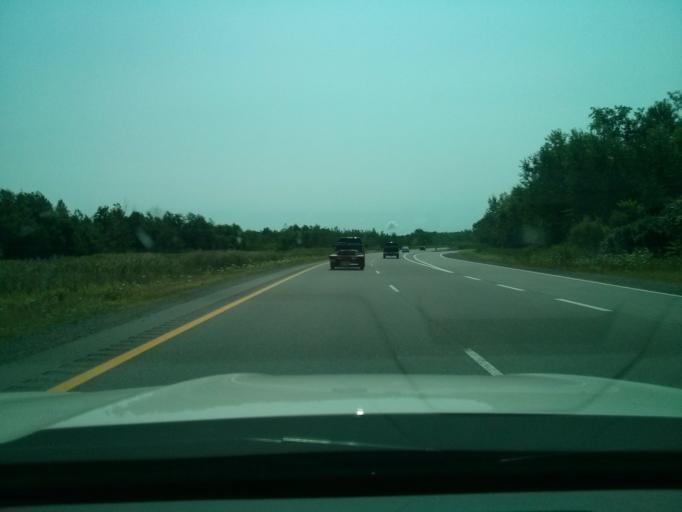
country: CA
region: Ontario
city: Bells Corners
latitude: 45.0808
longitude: -75.6330
